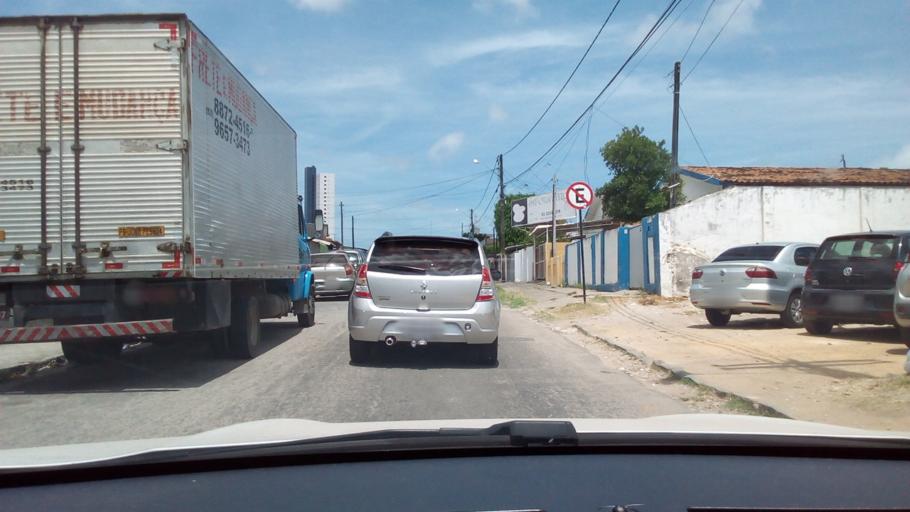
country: BR
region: Paraiba
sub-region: Joao Pessoa
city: Joao Pessoa
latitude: -7.1256
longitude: -34.8628
